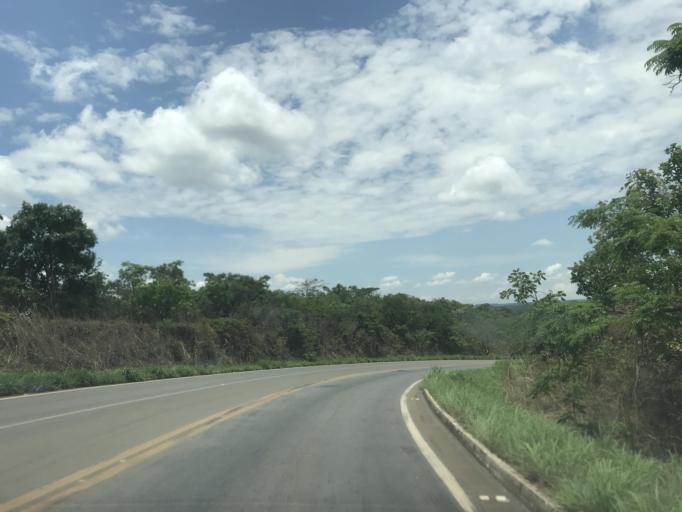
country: BR
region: Goias
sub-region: Luziania
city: Luziania
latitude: -16.3997
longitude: -48.1715
